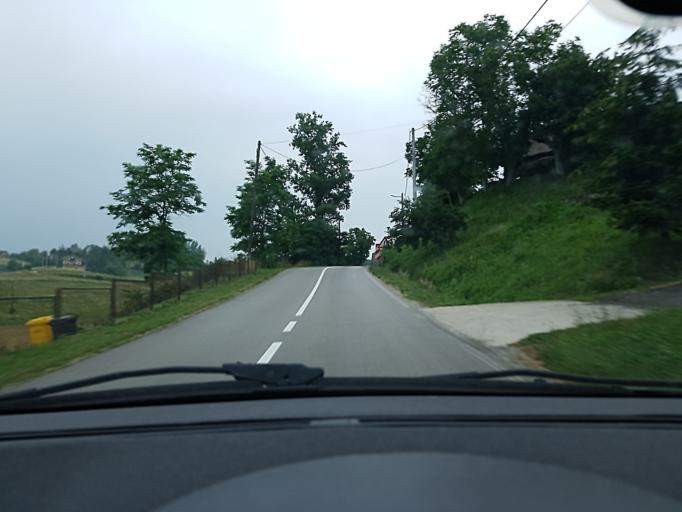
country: HR
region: Zagrebacka
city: Jakovlje
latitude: 45.9728
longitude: 15.8323
